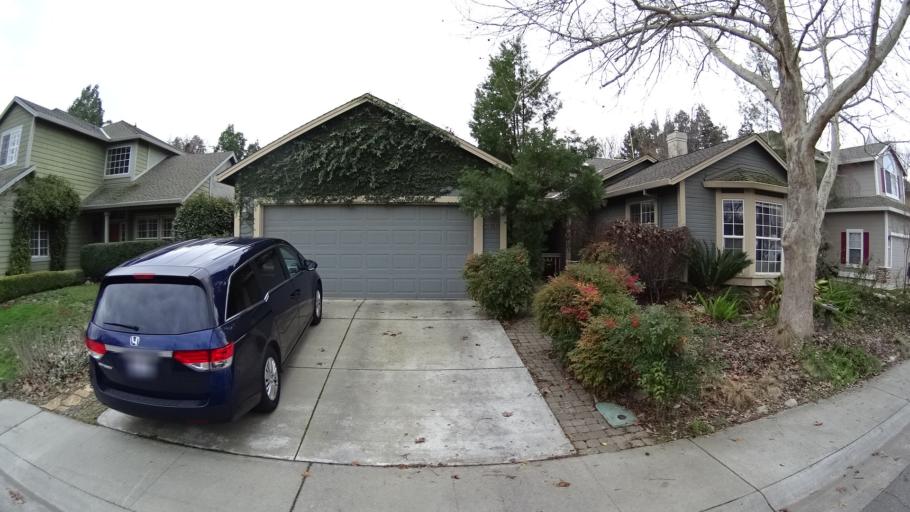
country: US
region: California
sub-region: Yolo County
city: Davis
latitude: 38.5557
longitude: -121.7188
